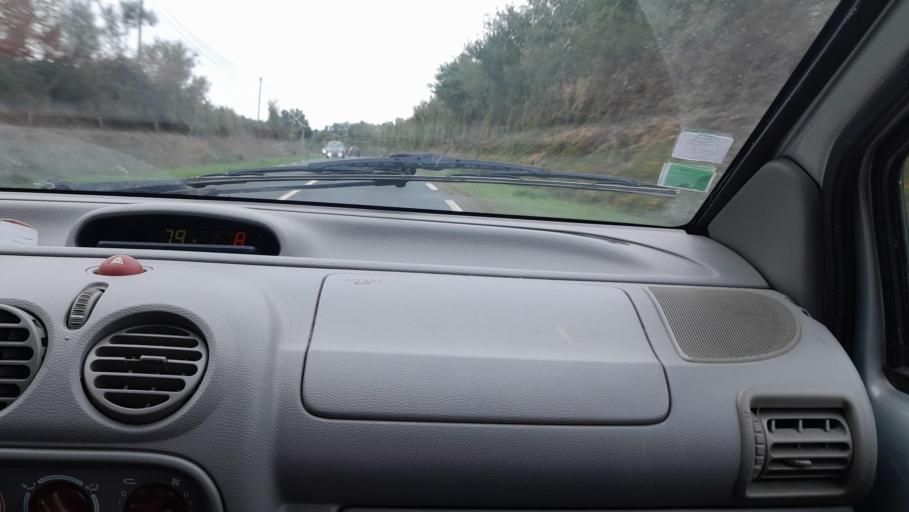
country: FR
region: Pays de la Loire
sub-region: Departement de la Loire-Atlantique
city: Saint-Mars-la-Jaille
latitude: 47.4961
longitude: -1.1741
